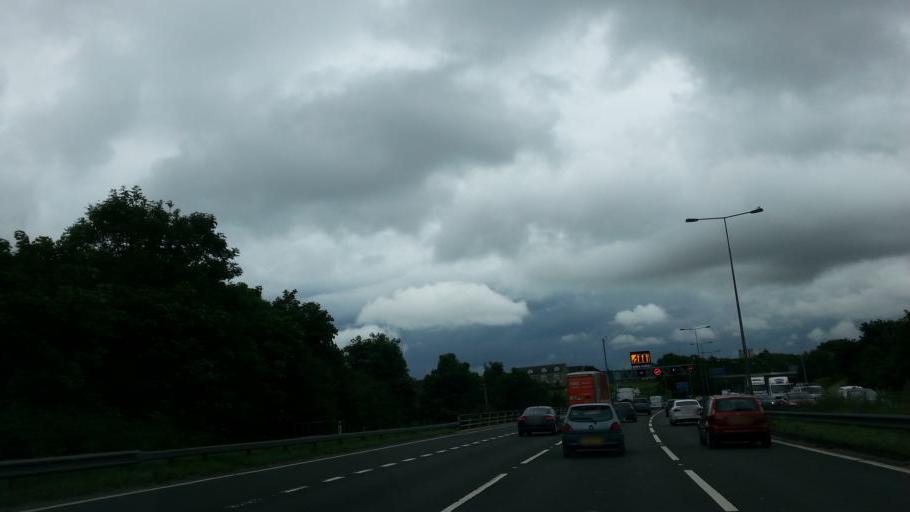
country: GB
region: England
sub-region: City and Borough of Leeds
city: Gildersome
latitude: 53.7457
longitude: -1.6300
